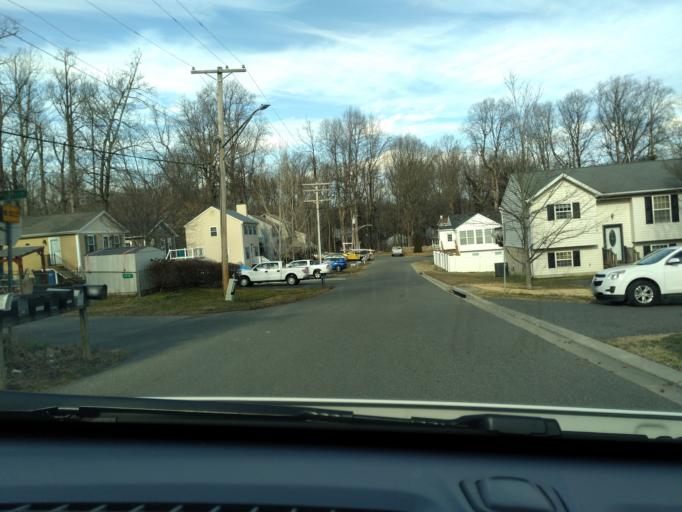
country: US
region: Maryland
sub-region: Calvert County
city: North Beach
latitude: 38.7113
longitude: -76.5432
